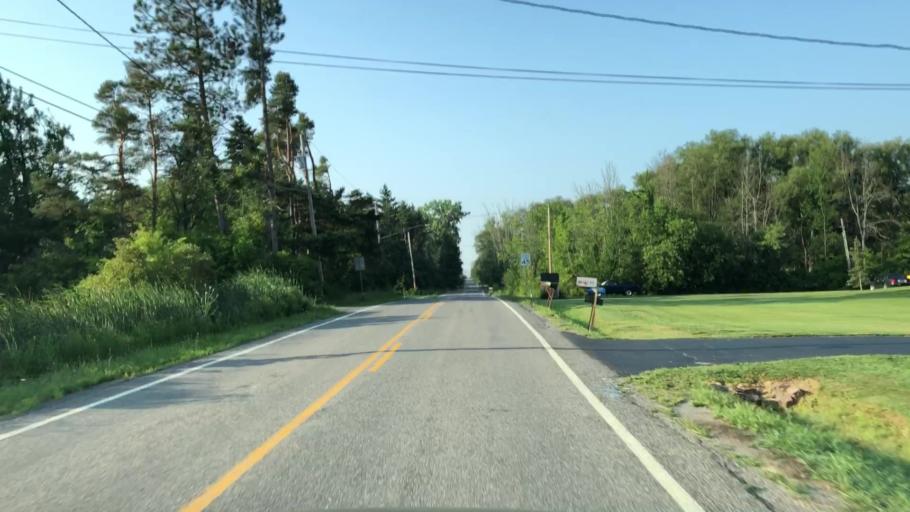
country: US
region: New York
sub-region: Erie County
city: Depew
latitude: 42.8527
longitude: -78.6924
